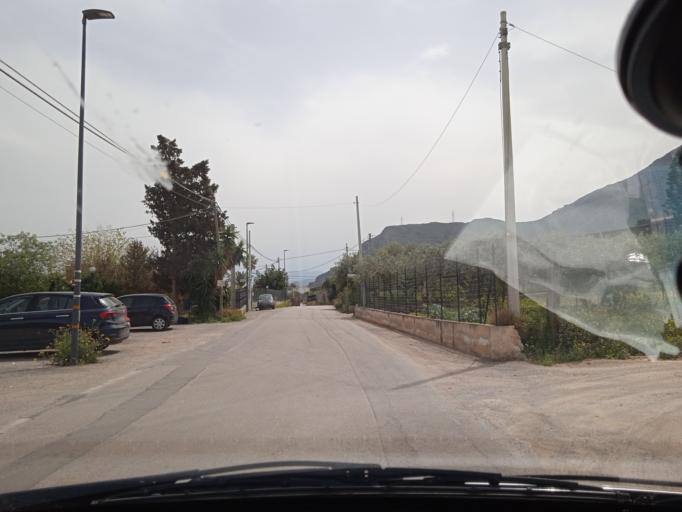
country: IT
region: Sicily
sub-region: Palermo
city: Torre Colonna-Sperone
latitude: 38.0318
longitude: 13.5663
